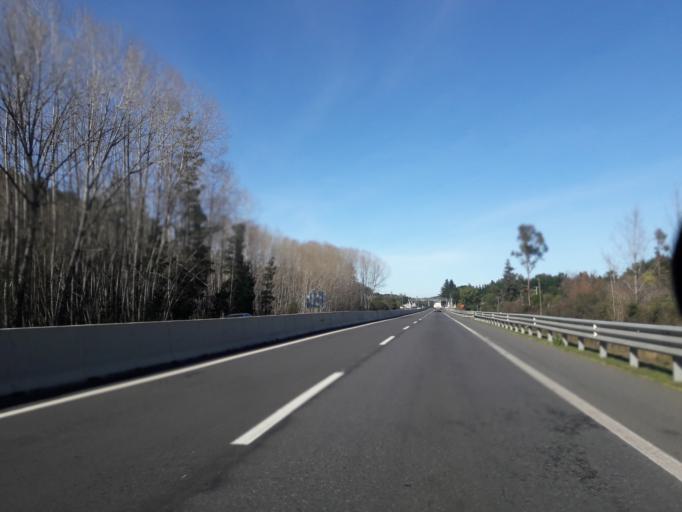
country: CL
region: Biobio
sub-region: Provincia de Biobio
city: Yumbel
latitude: -36.9471
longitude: -72.7522
